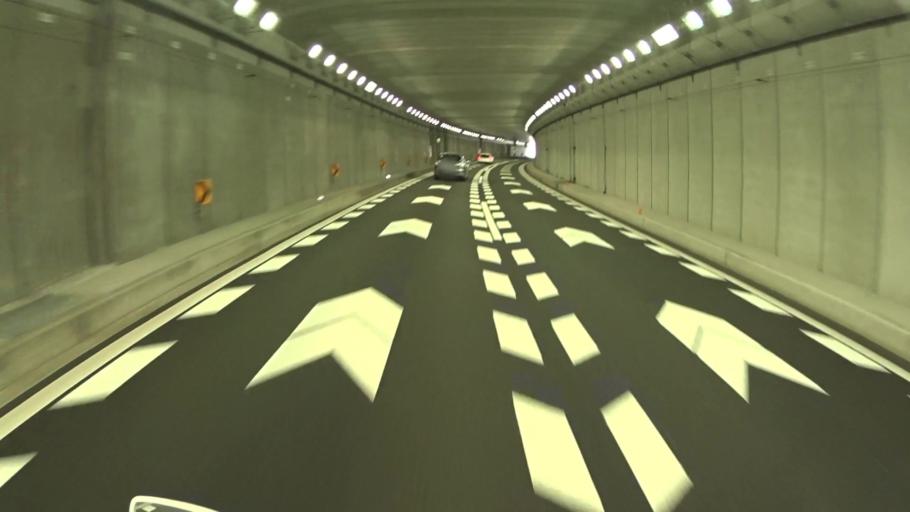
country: JP
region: Kyoto
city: Muko
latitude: 34.9560
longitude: 135.6551
